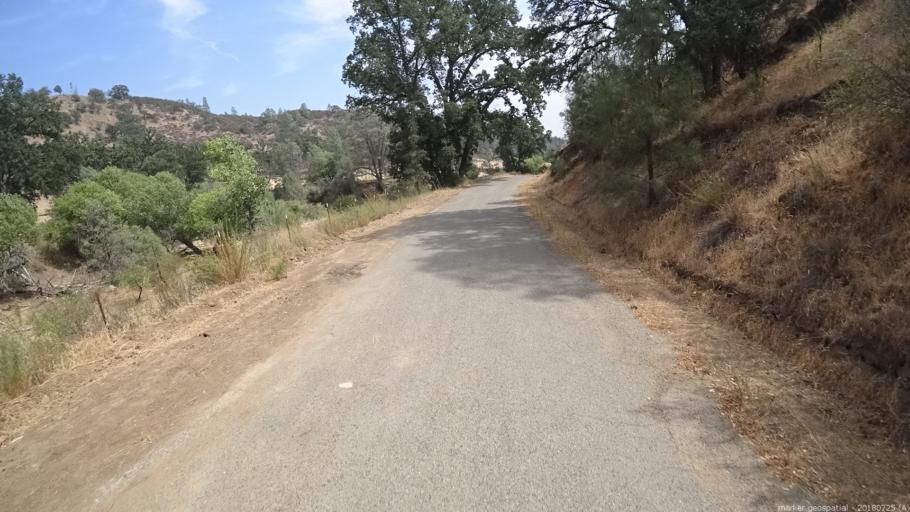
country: US
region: California
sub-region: Fresno County
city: Coalinga
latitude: 36.2250
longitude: -120.7073
